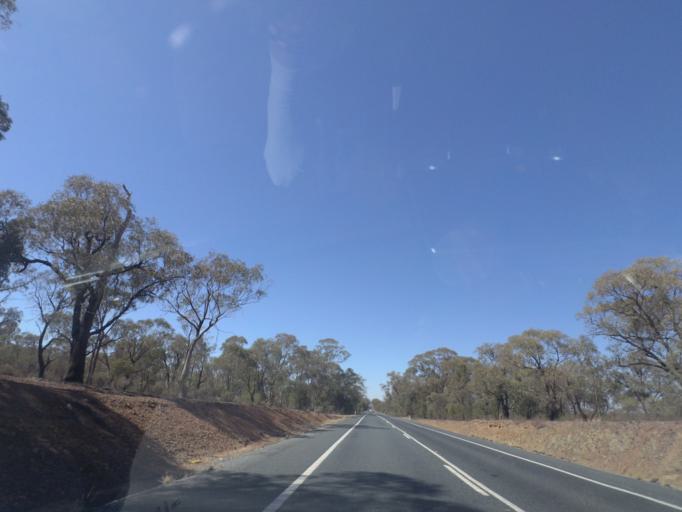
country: AU
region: New South Wales
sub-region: Bland
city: West Wyalong
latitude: -34.1677
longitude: 147.1156
